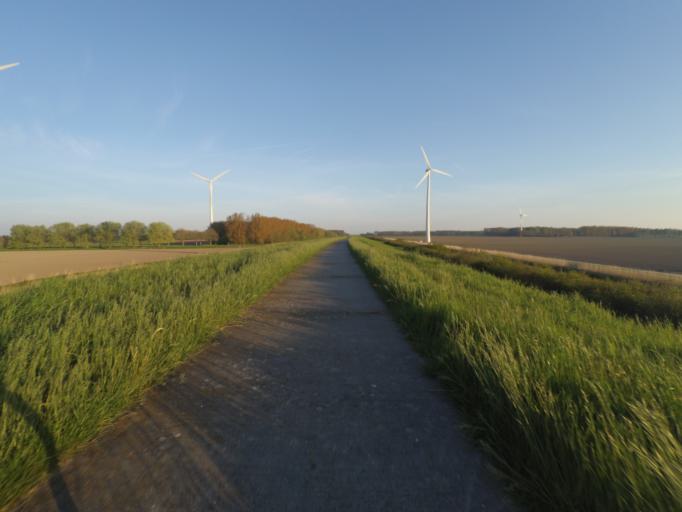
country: NL
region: Flevoland
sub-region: Gemeente Zeewolde
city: Zeewolde
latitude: 52.3978
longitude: 5.5098
